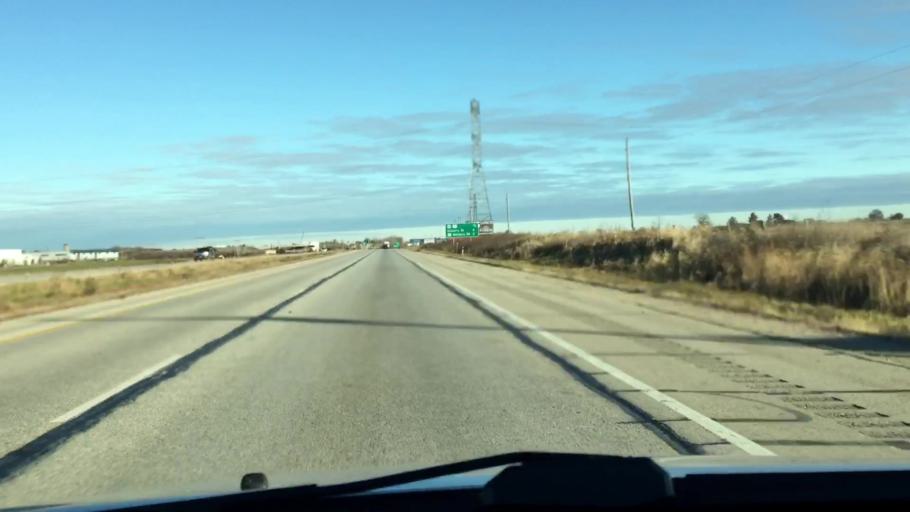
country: US
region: Wisconsin
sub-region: Fond du Lac County
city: Fond du Lac
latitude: 43.7238
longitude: -88.4422
